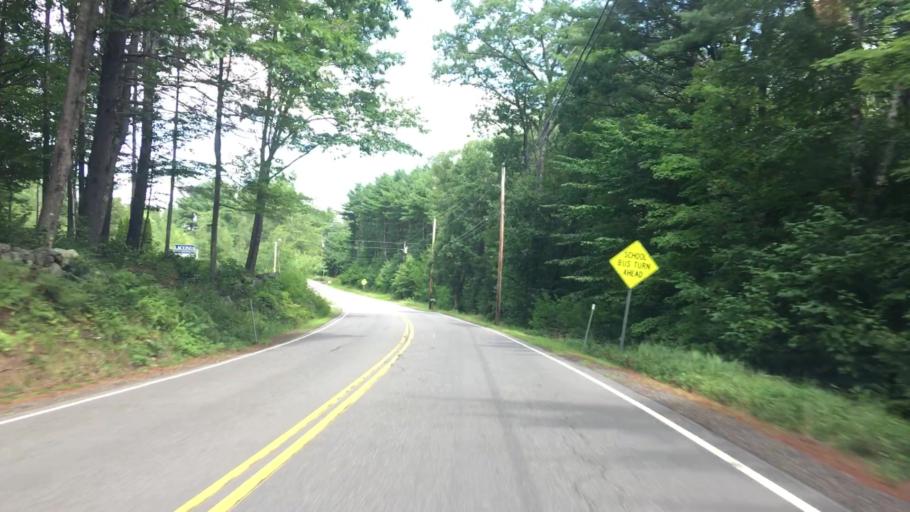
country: US
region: New Hampshire
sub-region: Belknap County
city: Meredith
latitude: 43.5989
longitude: -71.5181
